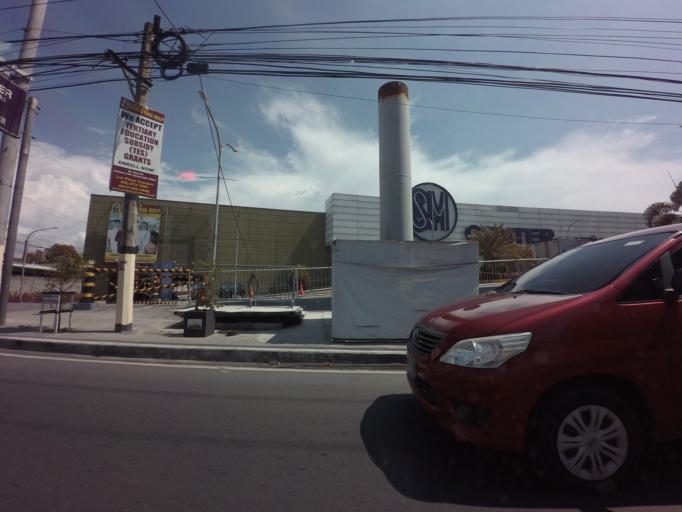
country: PH
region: Calabarzon
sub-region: Province of Rizal
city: Las Pinas
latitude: 14.4495
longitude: 120.9813
